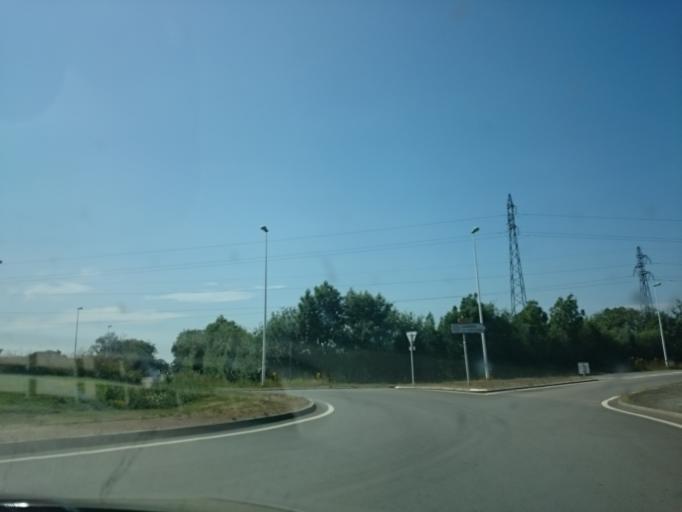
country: FR
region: Pays de la Loire
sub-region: Departement de la Loire-Atlantique
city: Indre
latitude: 47.2072
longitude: -1.6836
